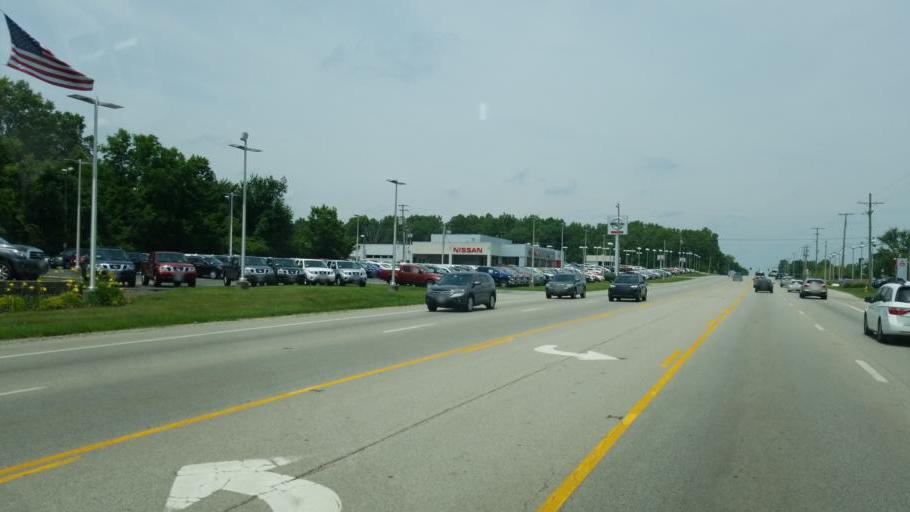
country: US
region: Ohio
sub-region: Franklin County
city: Worthington
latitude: 40.1390
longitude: -83.0171
